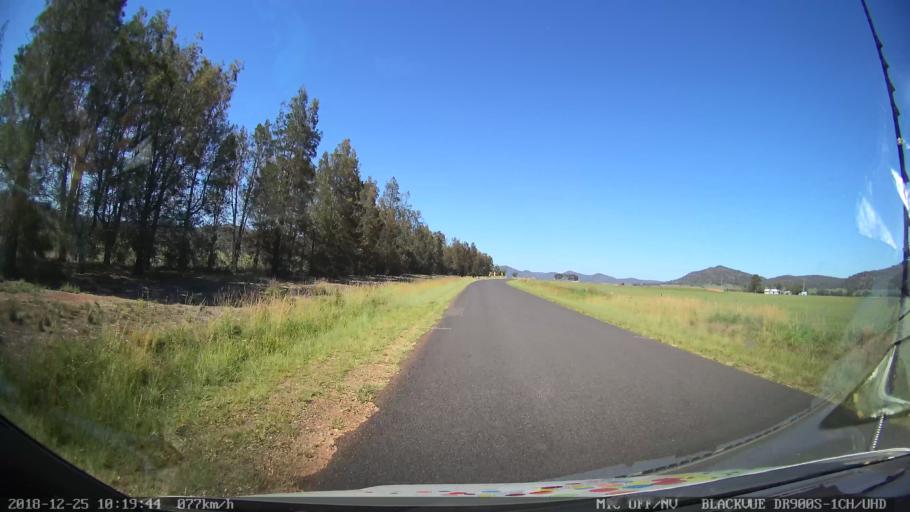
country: AU
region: New South Wales
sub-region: Muswellbrook
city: Denman
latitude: -32.3535
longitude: 150.5562
